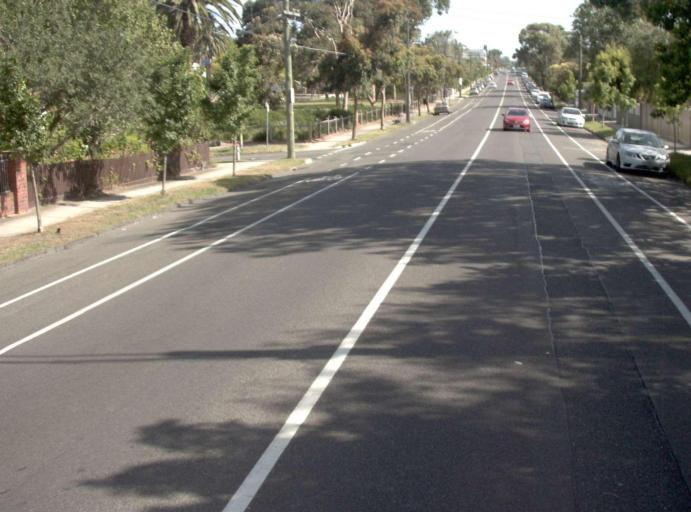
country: AU
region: Victoria
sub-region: Stonnington
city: Malvern East
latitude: -37.8607
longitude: 145.0407
